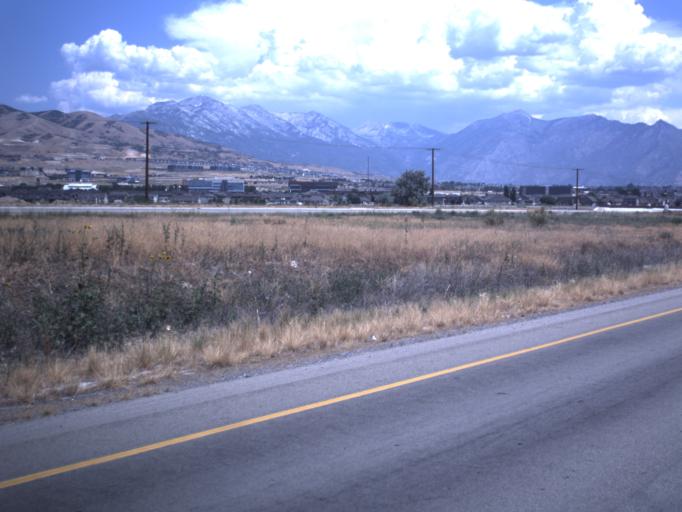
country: US
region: Utah
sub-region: Utah County
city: Lehi
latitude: 40.4124
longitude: -111.9019
